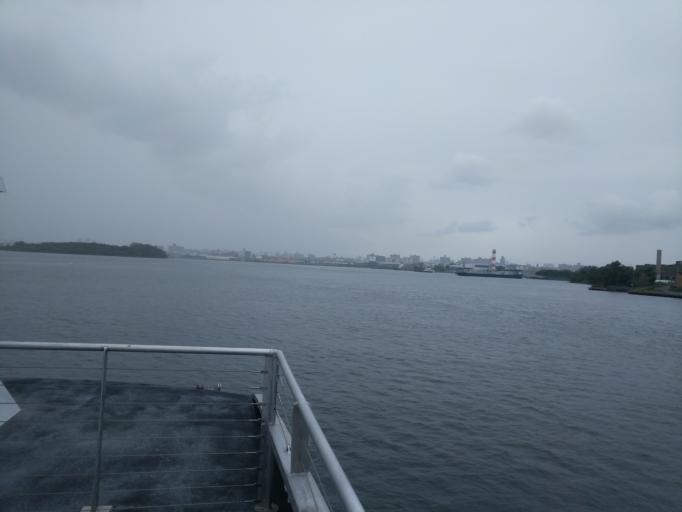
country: US
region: New York
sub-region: Bronx
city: The Bronx
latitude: 40.8003
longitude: -73.8834
